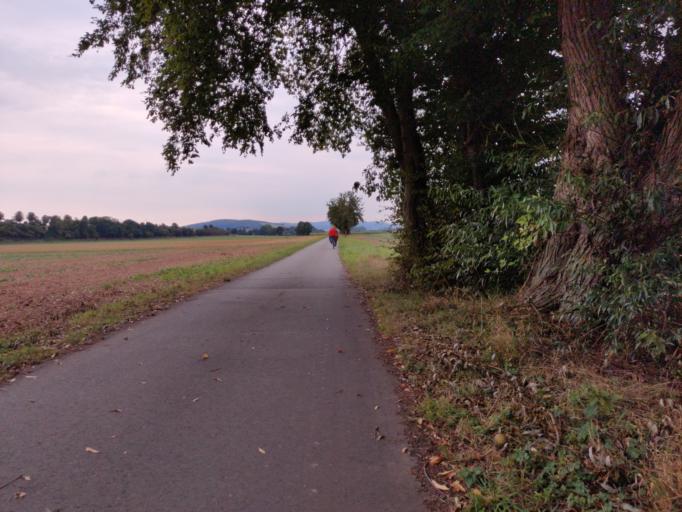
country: DE
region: Lower Saxony
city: Hehlen
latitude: 52.0427
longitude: 9.4138
